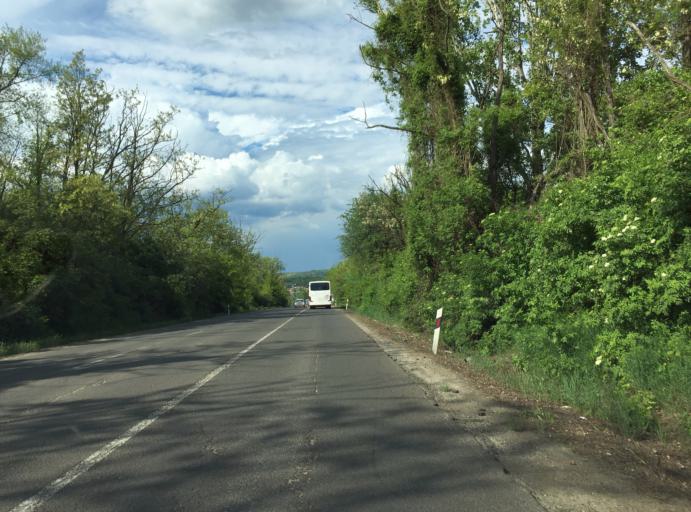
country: HU
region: Pest
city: Aszod
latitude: 47.6393
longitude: 19.4626
